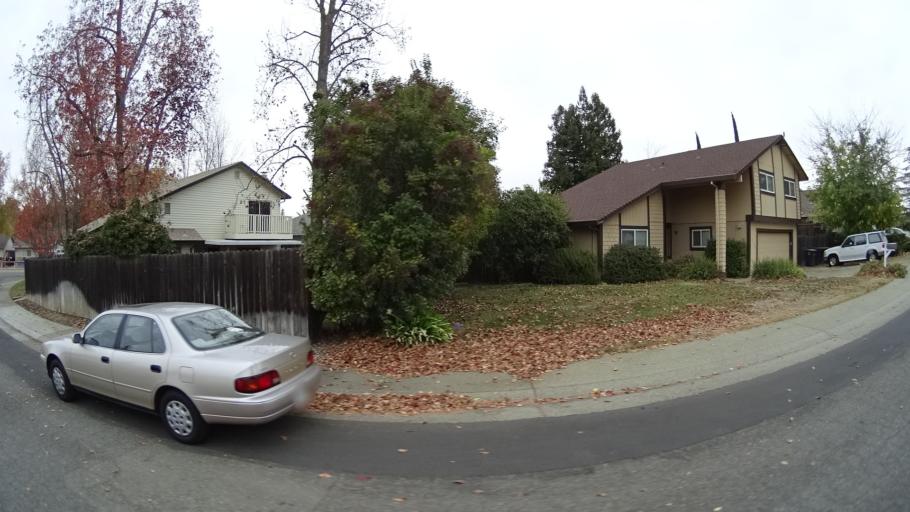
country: US
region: California
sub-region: Sacramento County
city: Citrus Heights
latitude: 38.7005
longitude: -121.3013
